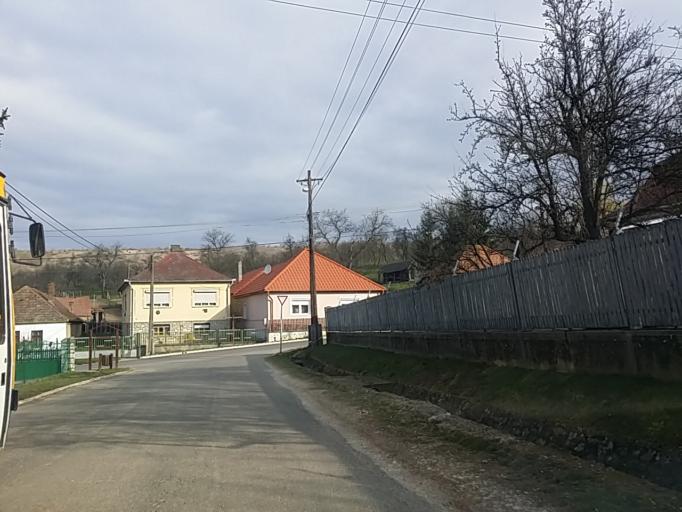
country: HU
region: Borsod-Abauj-Zemplen
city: Rudabanya
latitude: 48.4689
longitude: 20.5052
